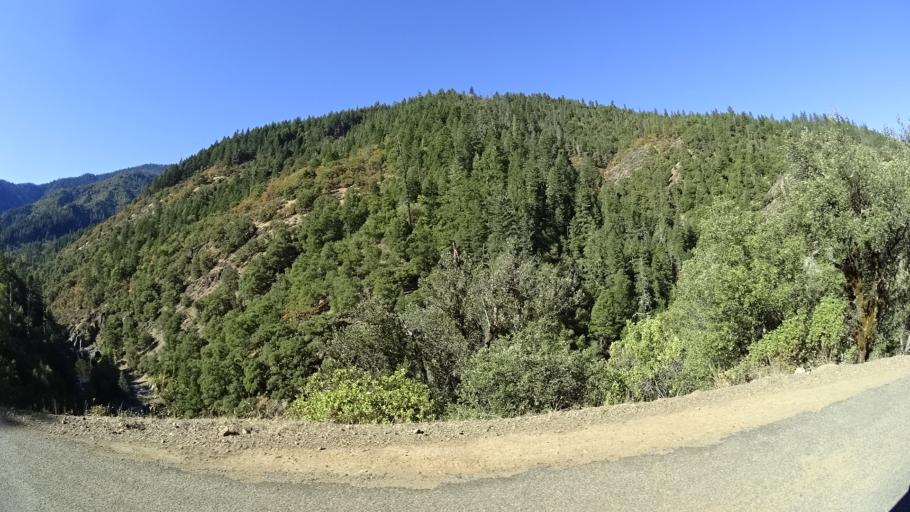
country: US
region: California
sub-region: Humboldt County
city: Willow Creek
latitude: 41.1839
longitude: -123.2173
